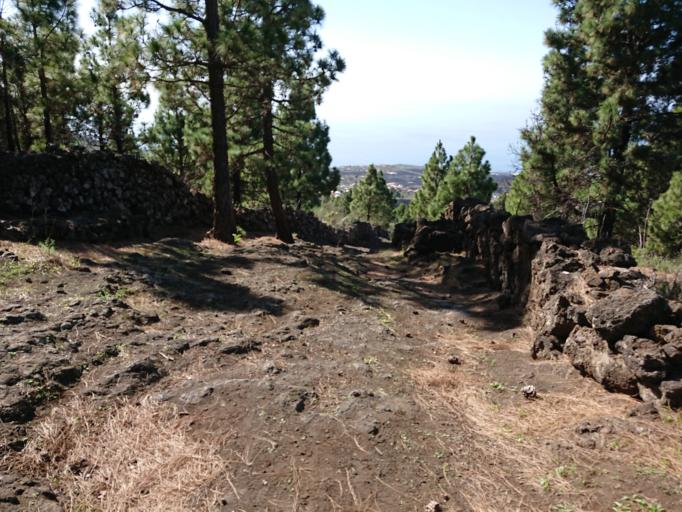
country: ES
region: Canary Islands
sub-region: Provincia de Santa Cruz de Tenerife
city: El Paso
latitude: 28.6057
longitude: -17.8702
